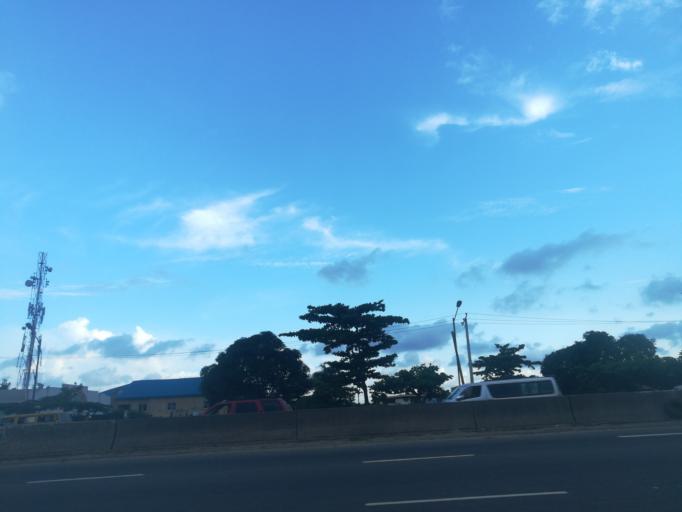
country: NG
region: Lagos
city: Somolu
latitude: 6.5482
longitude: 3.3844
